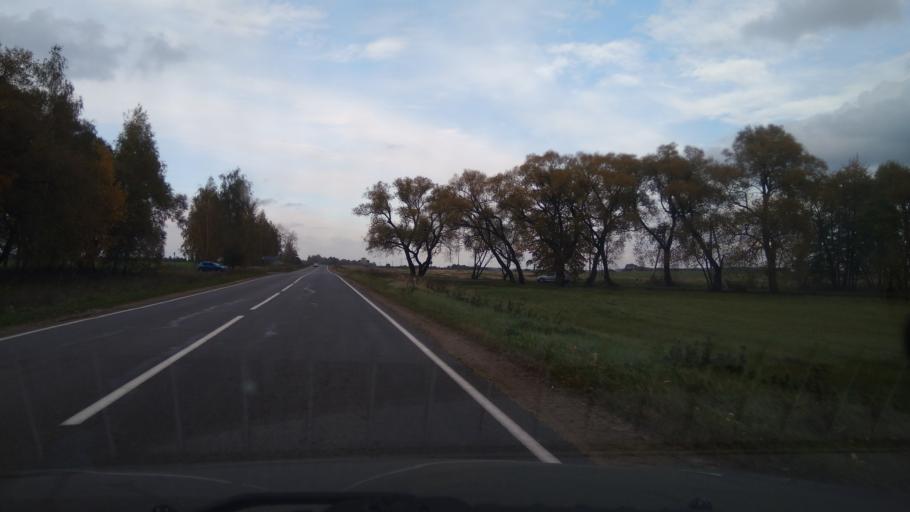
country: BY
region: Minsk
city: Dukora
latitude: 53.6807
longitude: 27.9568
